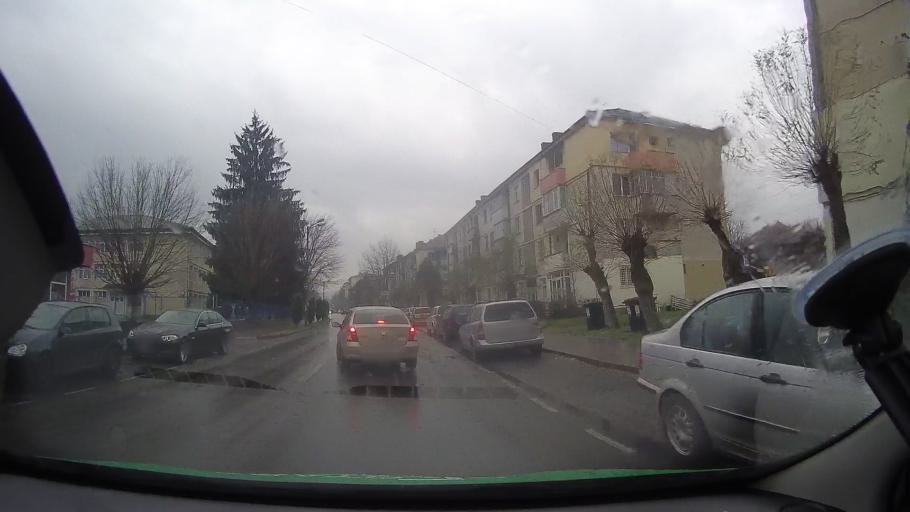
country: RO
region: Hunedoara
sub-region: Municipiul Brad
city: Brad
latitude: 46.1232
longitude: 22.7908
